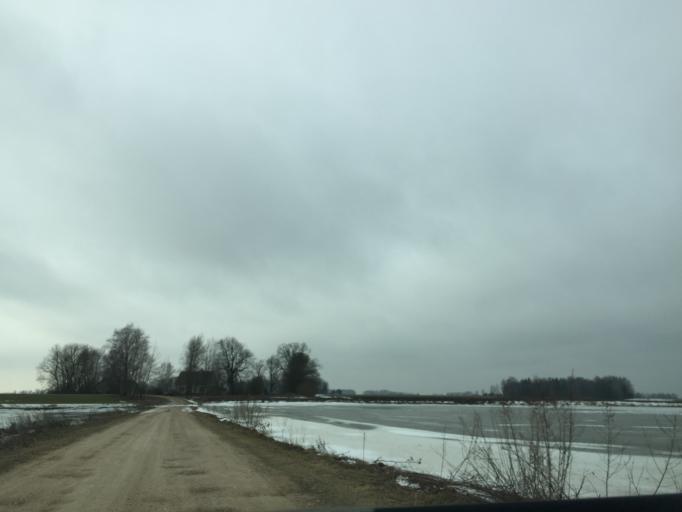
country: LV
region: Rundales
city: Pilsrundale
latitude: 56.5359
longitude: 23.9909
